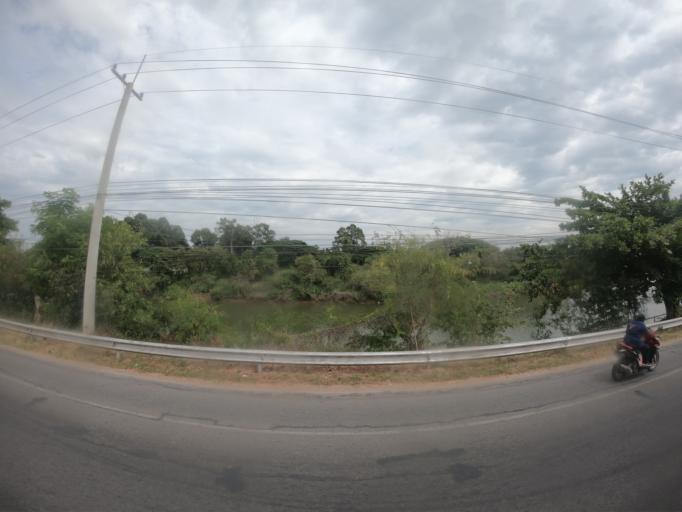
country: TH
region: Maha Sarakham
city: Maha Sarakham
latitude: 16.2184
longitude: 103.2760
